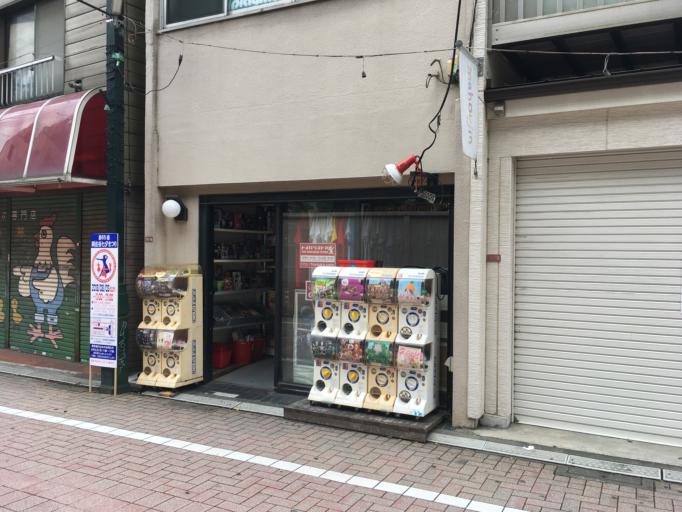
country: JP
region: Tokyo
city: Tokyo
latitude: 35.7069
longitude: 139.6357
